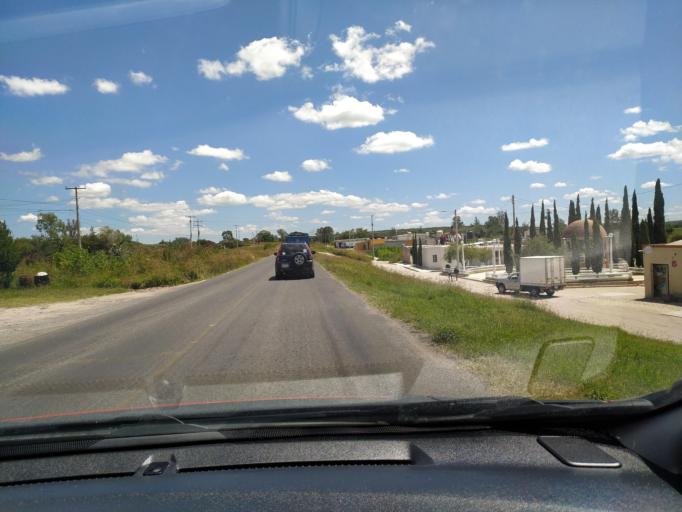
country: MX
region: Jalisco
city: San Diego de Alejandria
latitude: 21.0065
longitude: -102.0430
